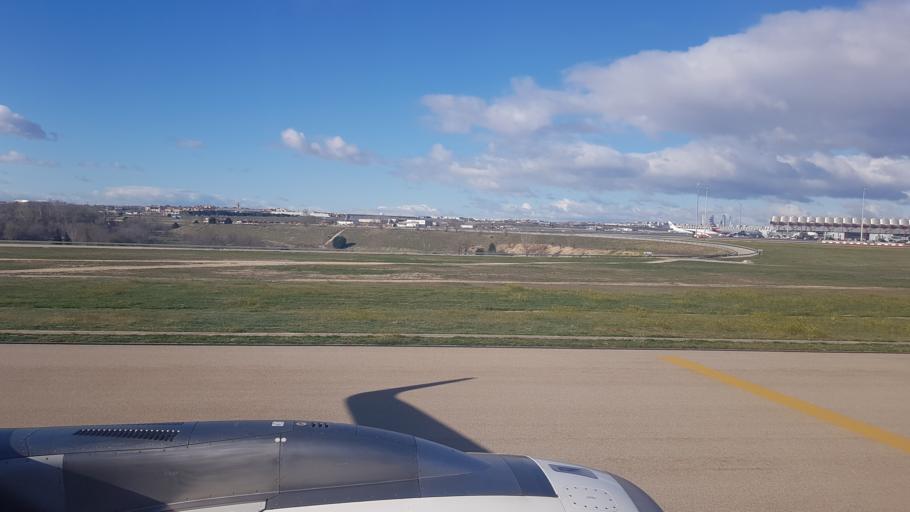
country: ES
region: Madrid
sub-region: Provincia de Madrid
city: Barajas de Madrid
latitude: 40.4907
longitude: -3.5566
